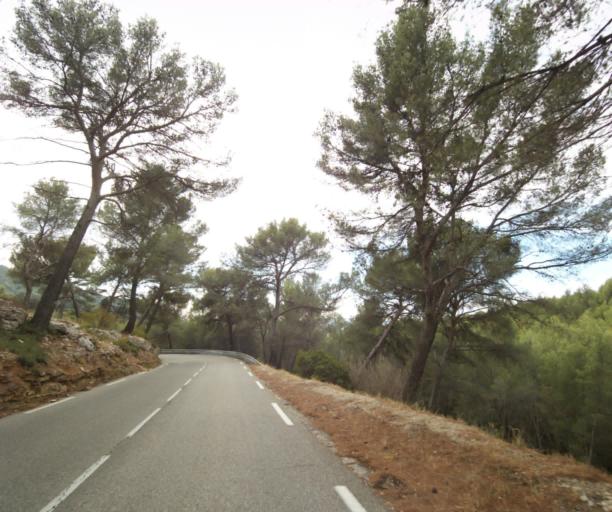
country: FR
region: Provence-Alpes-Cote d'Azur
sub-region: Departement des Bouches-du-Rhone
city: Ceyreste
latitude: 43.2269
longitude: 5.6480
